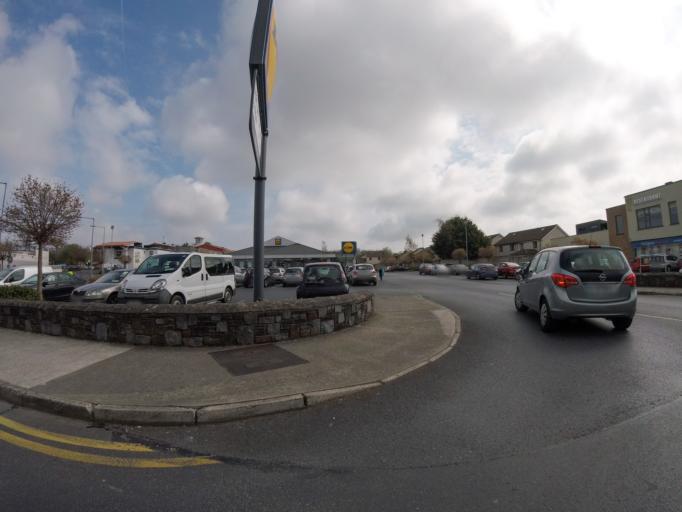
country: IE
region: Munster
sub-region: Waterford
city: Waterford
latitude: 52.2468
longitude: -7.0843
